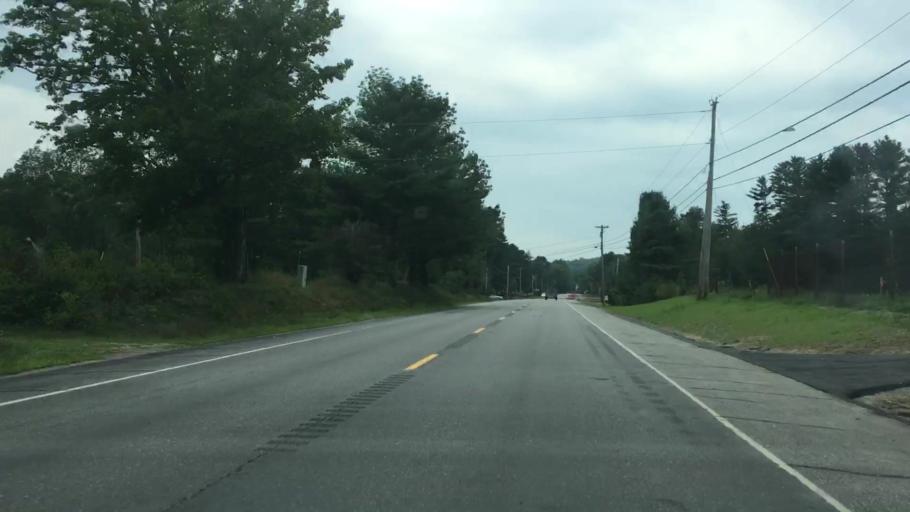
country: US
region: Maine
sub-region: Oxford County
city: Rumford
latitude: 44.5030
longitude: -70.6835
